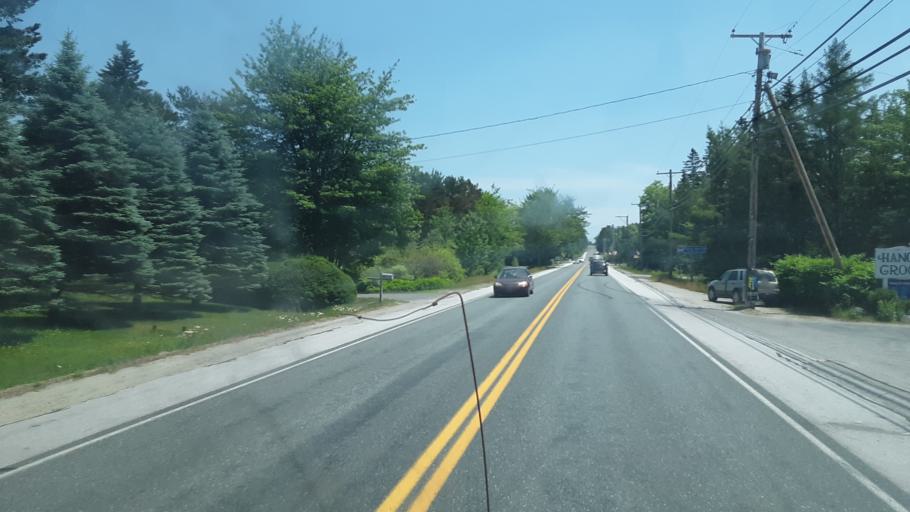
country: US
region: Maine
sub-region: Hancock County
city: Hancock
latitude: 44.5303
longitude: -68.2588
